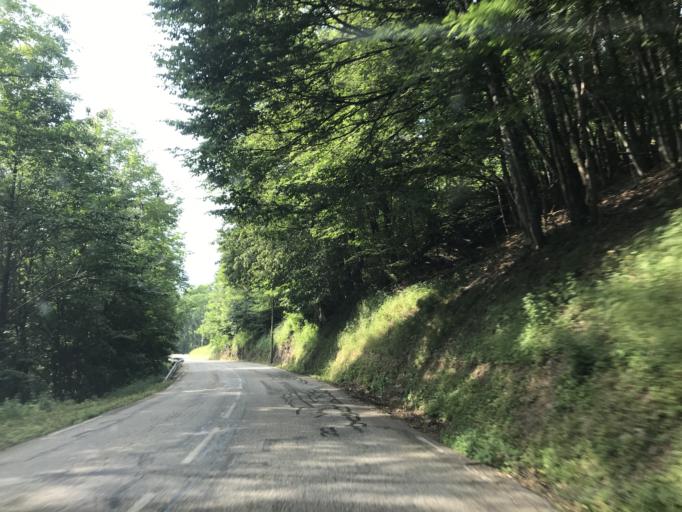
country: FR
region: Rhone-Alpes
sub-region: Departement de l'Isere
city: Allevard
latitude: 45.3866
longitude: 6.0850
